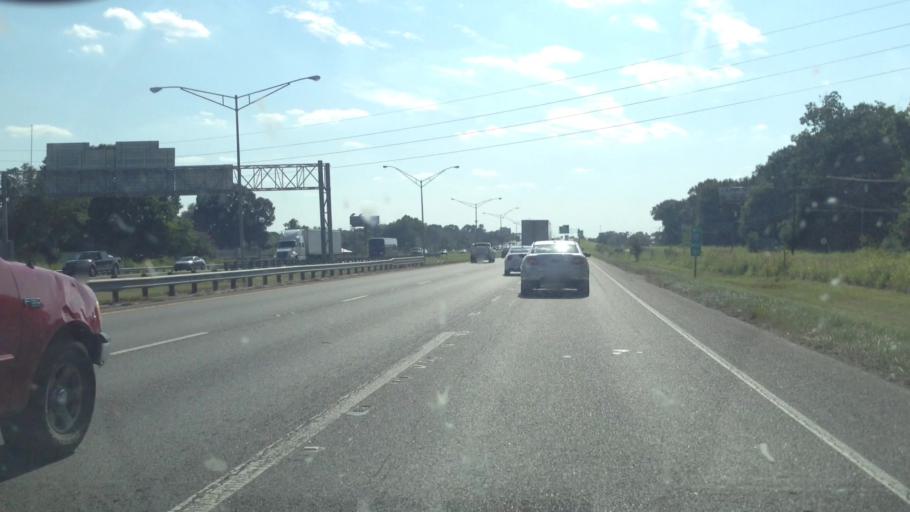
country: US
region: Louisiana
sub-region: Lafayette Parish
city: Lafayette
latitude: 30.2580
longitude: -92.0202
